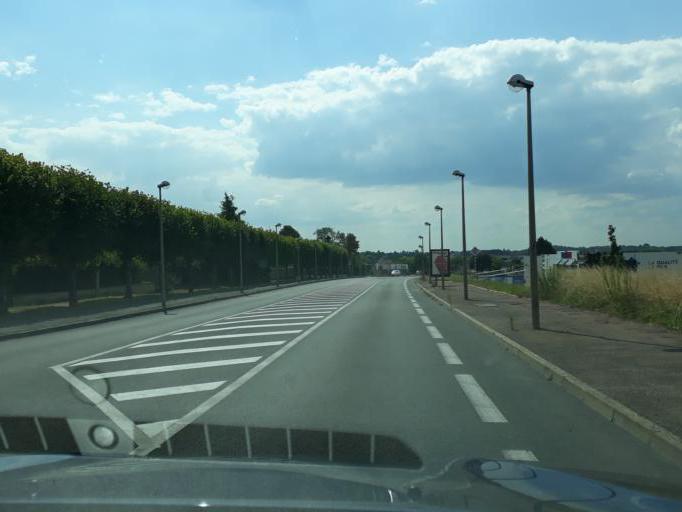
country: FR
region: Bourgogne
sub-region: Departement de la Nievre
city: Varennes-Vauzelles
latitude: 46.9963
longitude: 3.1264
